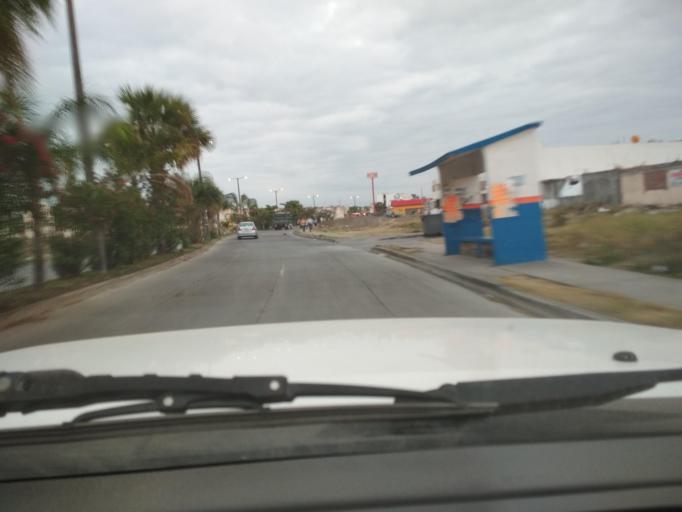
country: MX
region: Veracruz
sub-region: Medellin
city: Fraccionamiento Arboledas San Ramon
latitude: 19.0990
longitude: -96.1623
